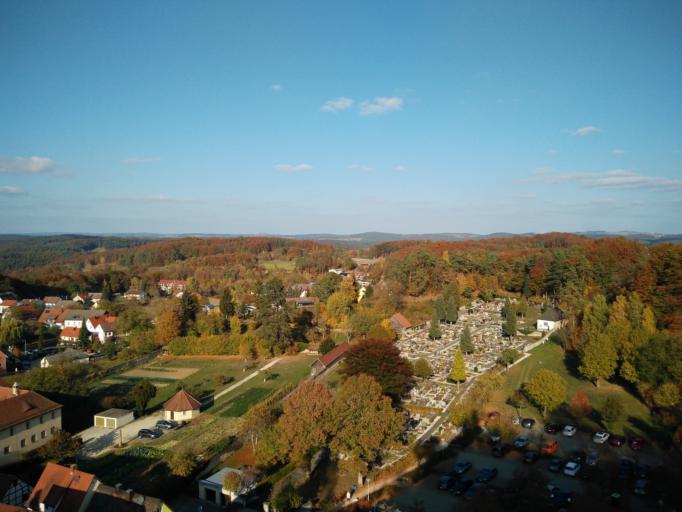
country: DE
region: Bavaria
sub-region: Upper Franconia
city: Gossweinstein
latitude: 49.7684
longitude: 11.3386
